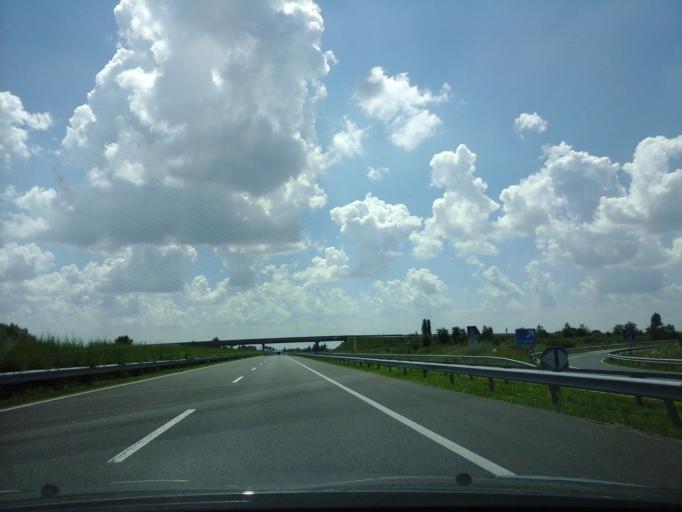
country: HU
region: Hajdu-Bihar
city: Debrecen
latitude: 47.5370
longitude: 21.5521
